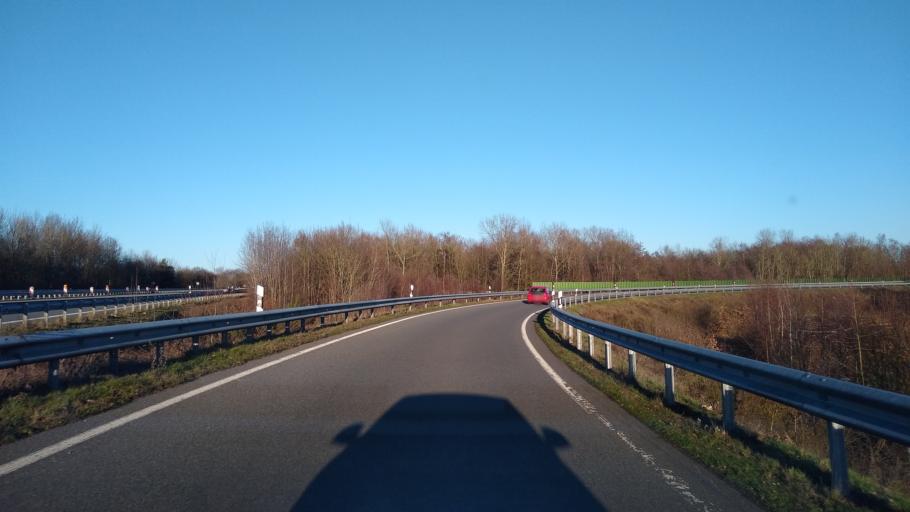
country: DE
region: Lower Saxony
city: Rastede
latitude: 53.2068
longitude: 8.2219
